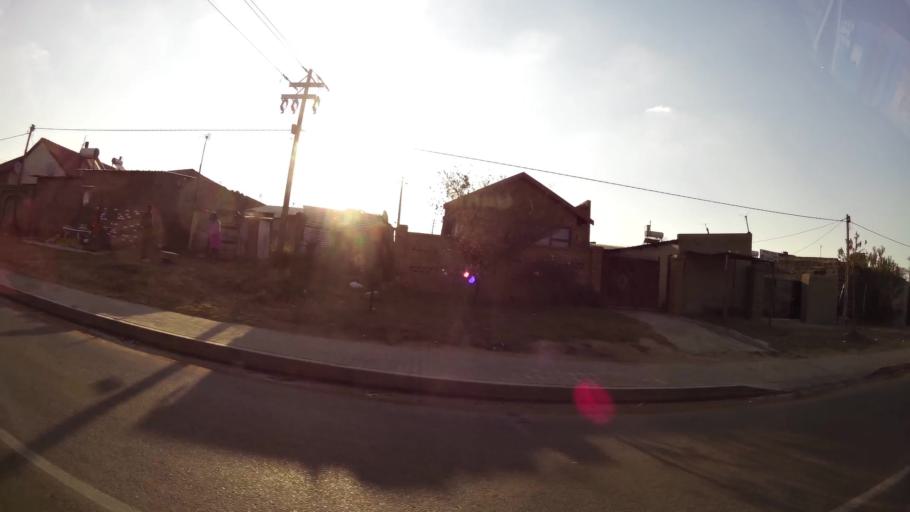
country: ZA
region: Gauteng
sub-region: Ekurhuleni Metropolitan Municipality
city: Tembisa
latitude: -26.0160
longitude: 28.1831
